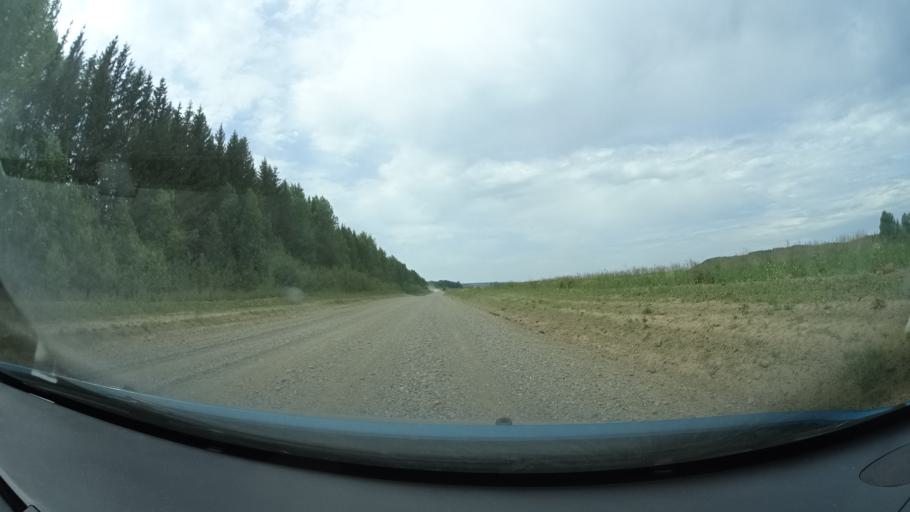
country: RU
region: Perm
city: Barda
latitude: 56.8119
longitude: 55.6542
